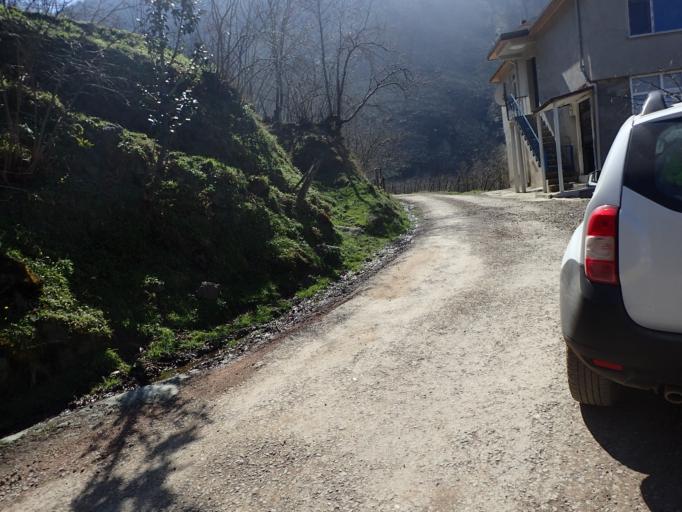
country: TR
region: Ordu
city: Catalpinar
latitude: 40.8636
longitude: 37.4943
